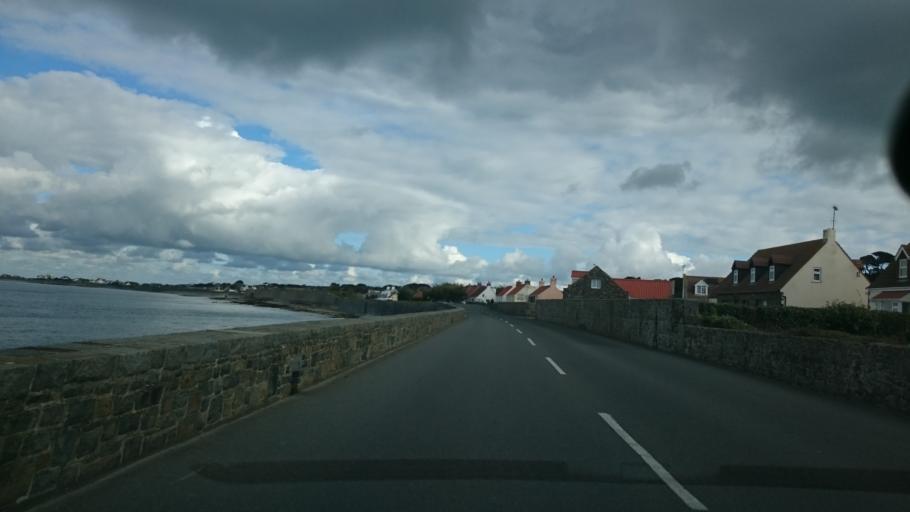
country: GG
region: St Peter Port
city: Saint Peter Port
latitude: 49.4403
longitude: -2.6518
